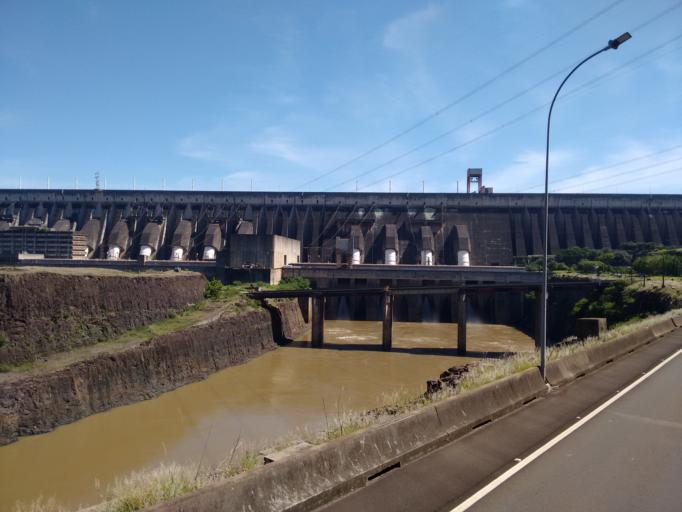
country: PY
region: Alto Parana
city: Ciudad del Este
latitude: -25.4132
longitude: -54.5870
